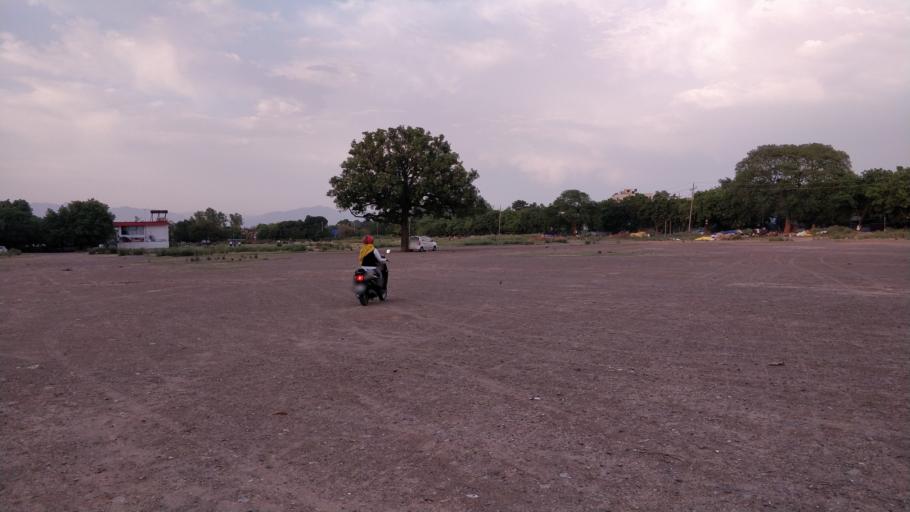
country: IN
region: Chandigarh
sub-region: Chandigarh
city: Chandigarh
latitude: 30.7190
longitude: 76.7690
